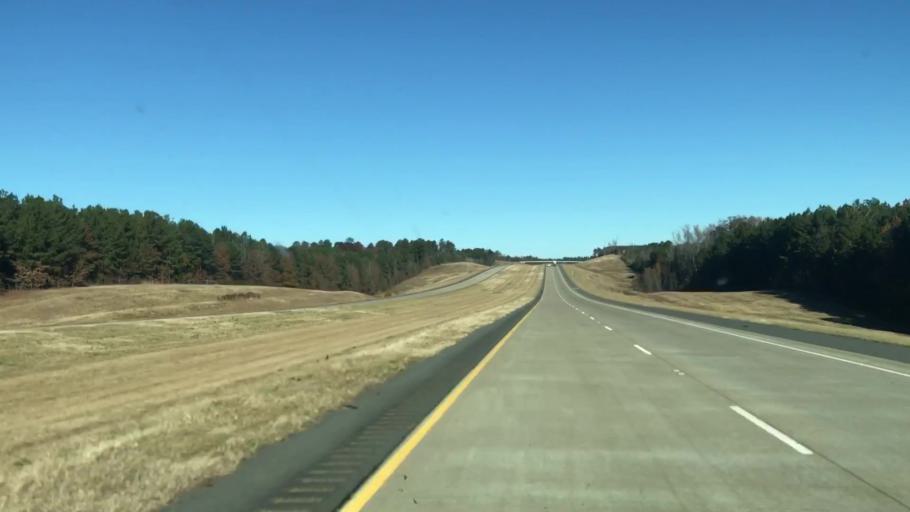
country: US
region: Louisiana
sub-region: Caddo Parish
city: Vivian
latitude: 32.9641
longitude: -93.9044
